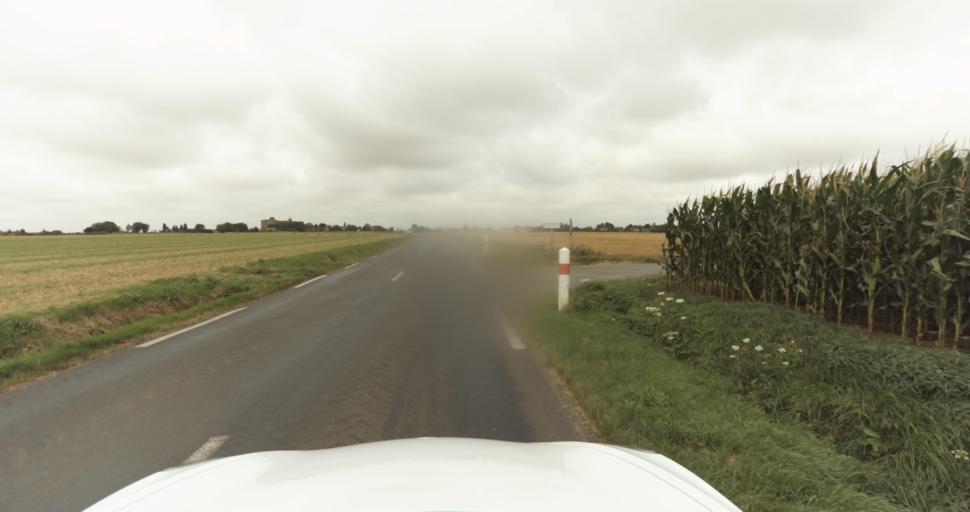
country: FR
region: Haute-Normandie
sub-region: Departement de l'Eure
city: Claville
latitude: 49.0860
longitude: 1.0487
